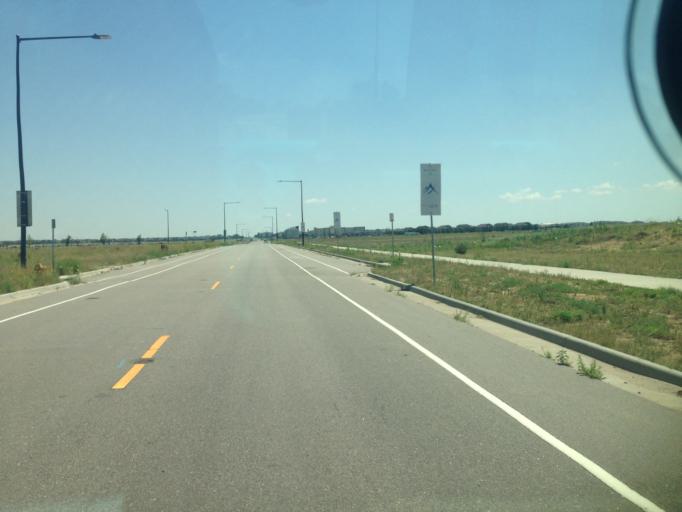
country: US
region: Colorado
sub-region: Adams County
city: Aurora
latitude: 39.8056
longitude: -104.7817
